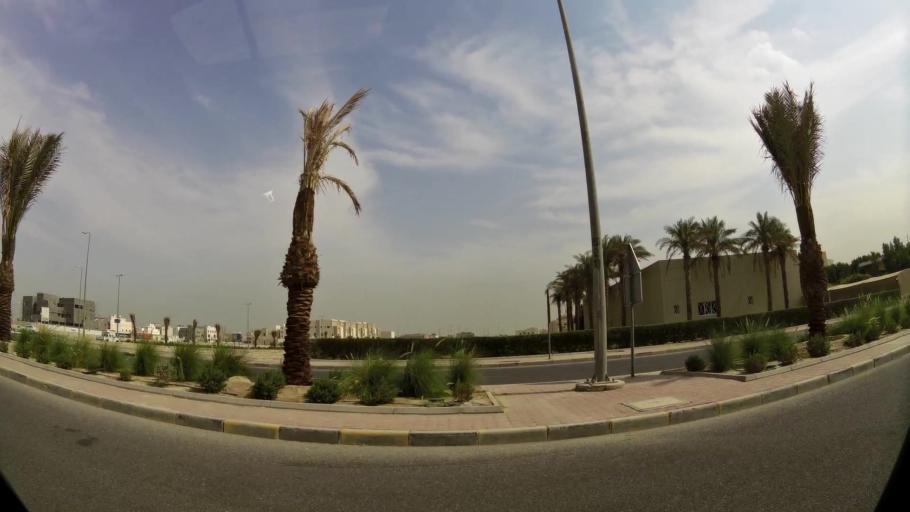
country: KW
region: Al Farwaniyah
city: Janub as Surrah
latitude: 29.2967
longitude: 47.9970
